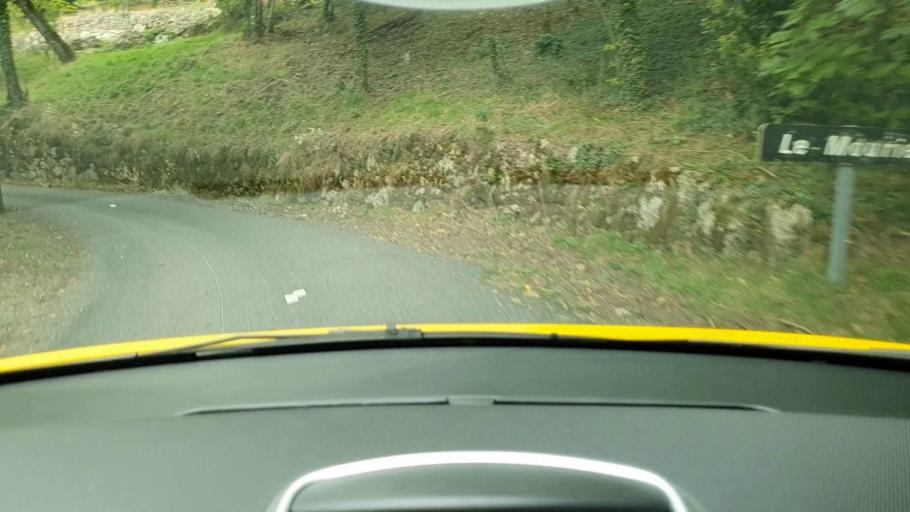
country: FR
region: Languedoc-Roussillon
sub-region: Departement de la Lozere
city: Meyrueis
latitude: 44.0577
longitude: 3.4290
